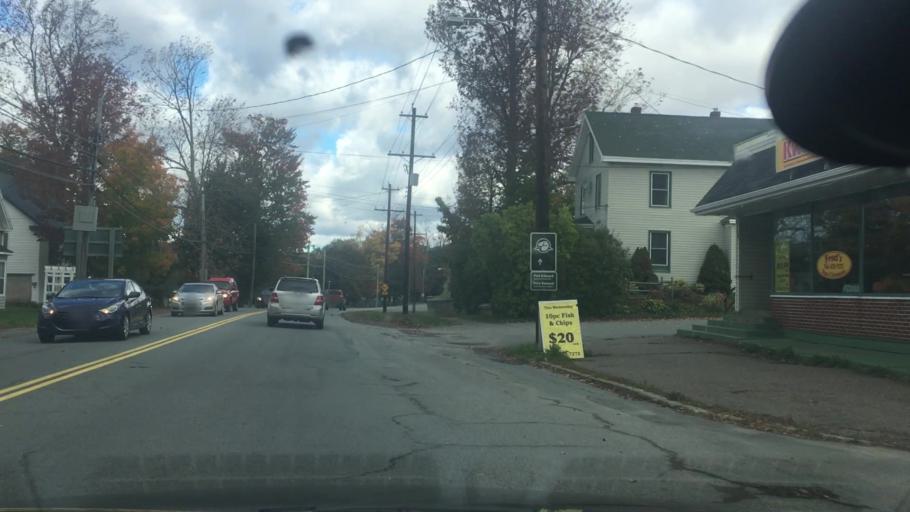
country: CA
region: Nova Scotia
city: Windsor
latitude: 44.9803
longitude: -64.1293
